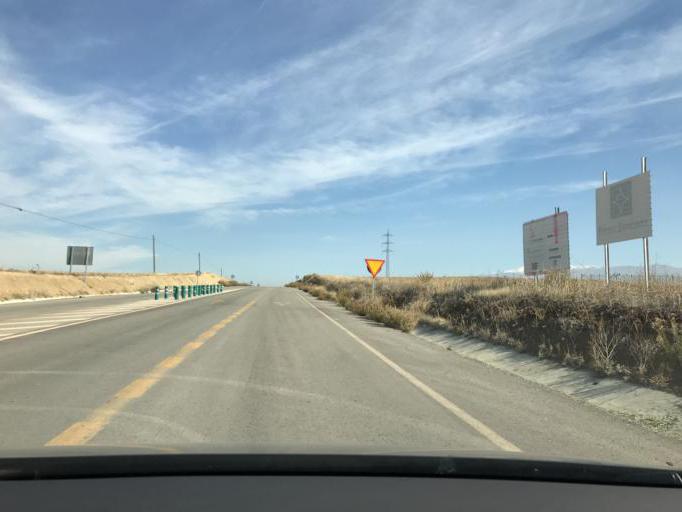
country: ES
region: Andalusia
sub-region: Provincia de Granada
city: Escuzar
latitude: 37.0875
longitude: -3.7503
